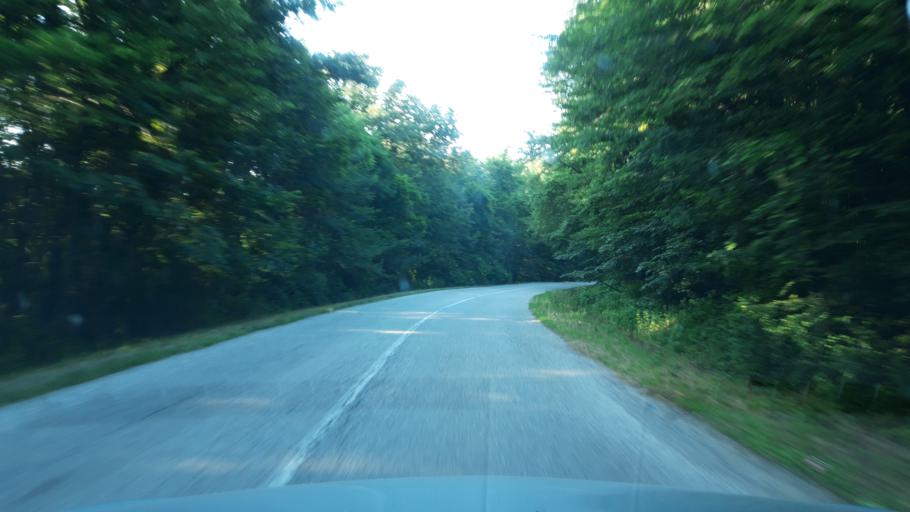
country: RS
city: Glozan
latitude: 45.1485
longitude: 19.5795
